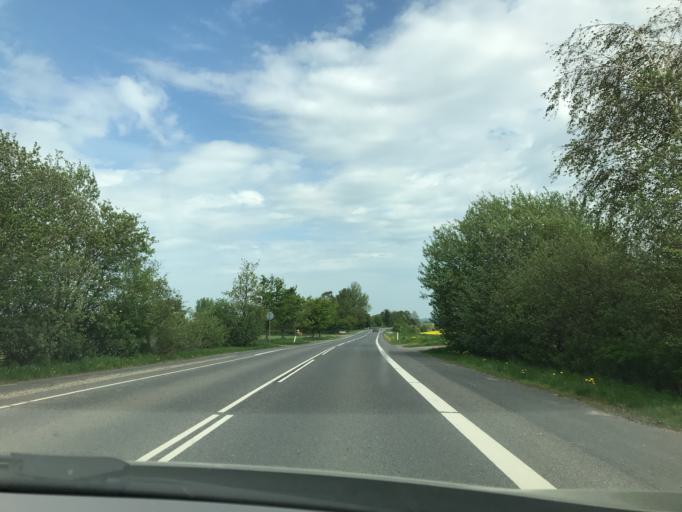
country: DK
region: South Denmark
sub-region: Assens Kommune
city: Assens
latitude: 55.2844
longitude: 9.9218
